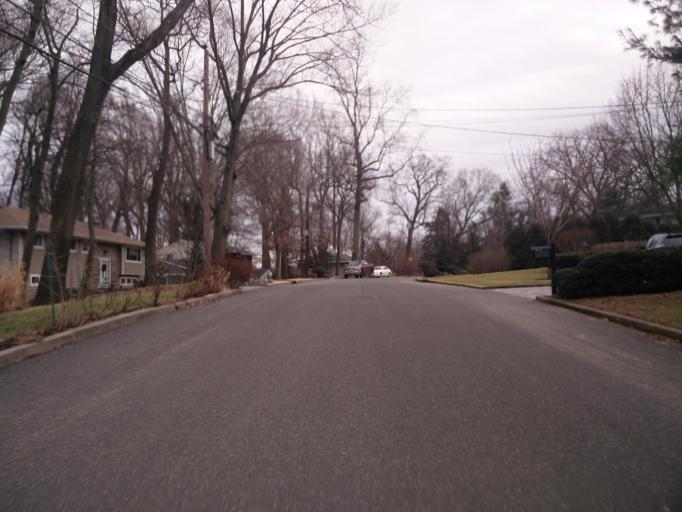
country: US
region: New York
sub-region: Nassau County
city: Lattingtown
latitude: 40.8818
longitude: -73.6190
